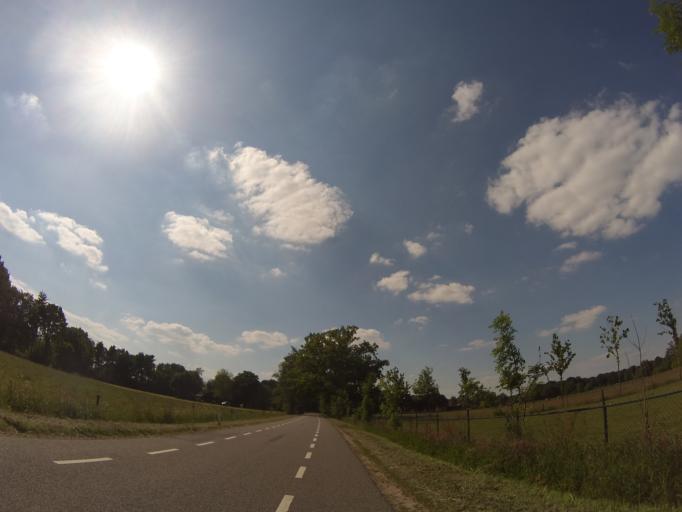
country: NL
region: Gelderland
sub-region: Gemeente Barneveld
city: Terschuur
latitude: 52.1507
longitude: 5.5305
